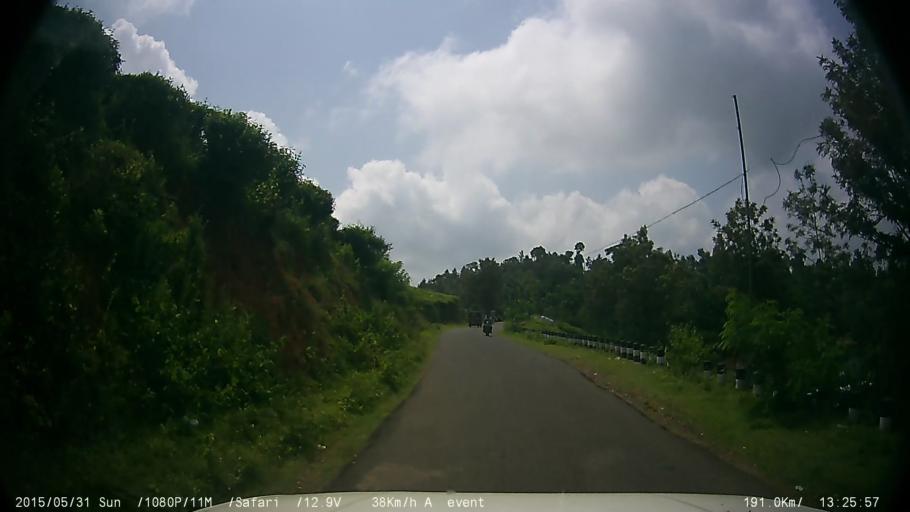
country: IN
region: Kerala
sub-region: Wayanad
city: Kalpetta
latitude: 11.5471
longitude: 76.1386
